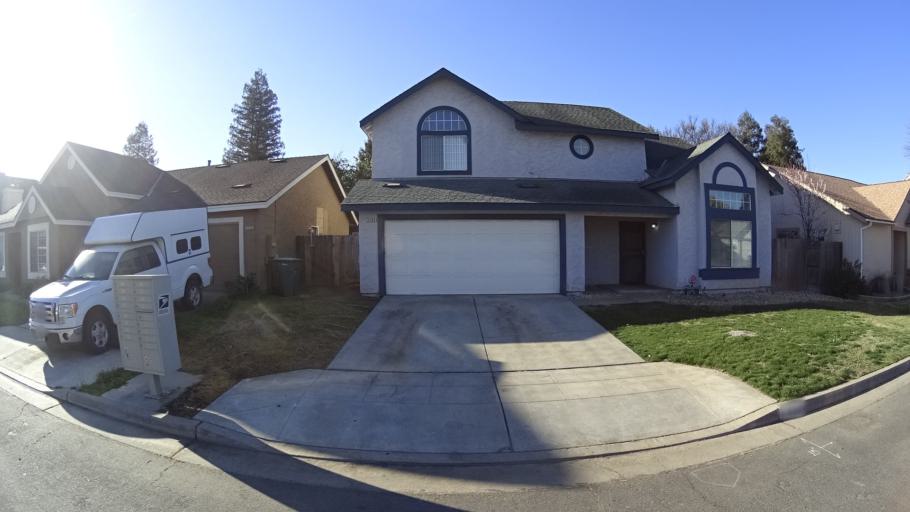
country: US
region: California
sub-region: Fresno County
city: Clovis
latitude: 36.8433
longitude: -119.7456
